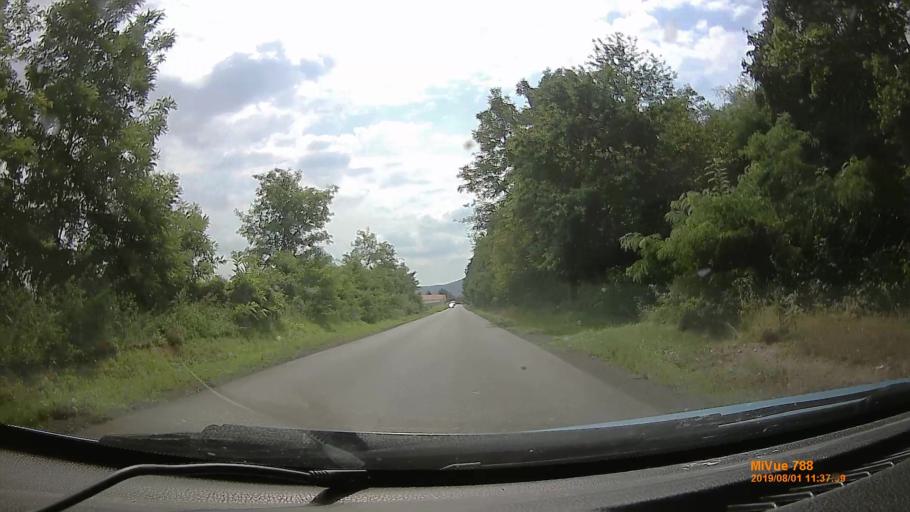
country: HU
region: Baranya
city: Villany
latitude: 45.9047
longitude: 18.3845
